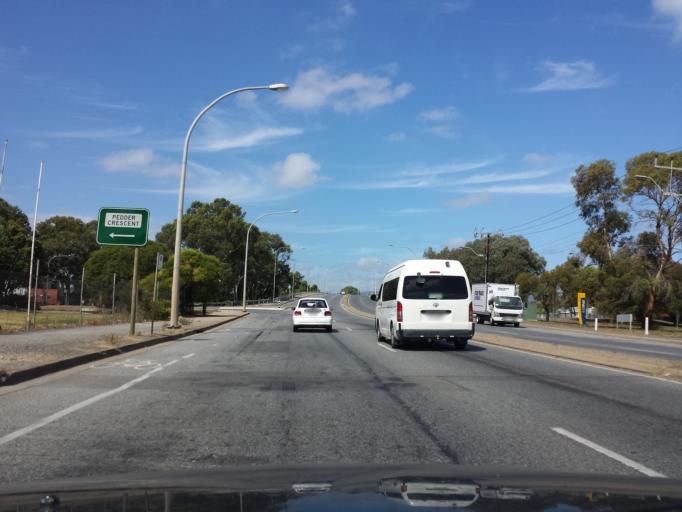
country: AU
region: South Australia
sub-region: Prospect
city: Prospect
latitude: -34.8747
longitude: 138.5780
